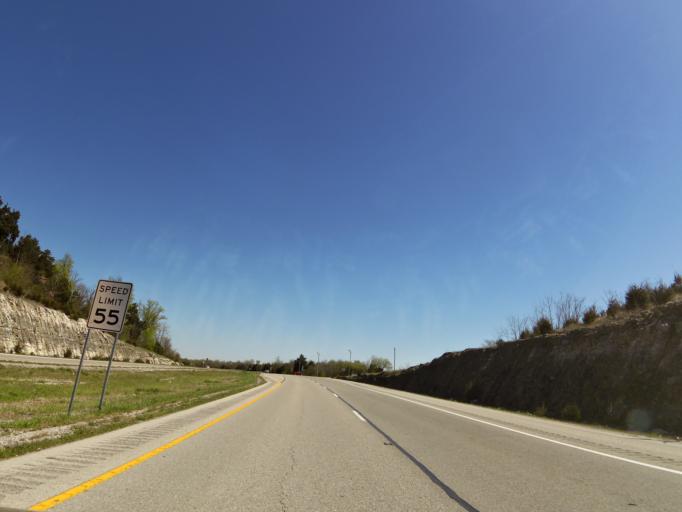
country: US
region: Kentucky
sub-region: Logan County
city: Auburn
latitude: 36.8587
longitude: -86.7420
